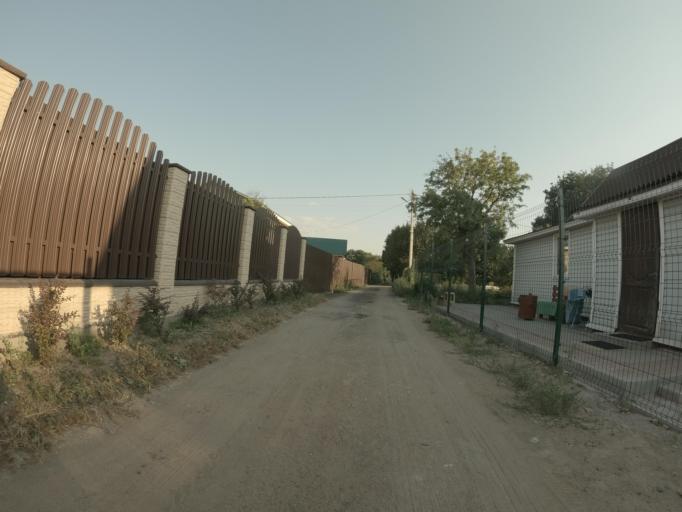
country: RU
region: Leningrad
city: Koltushi
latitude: 59.8900
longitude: 30.6979
